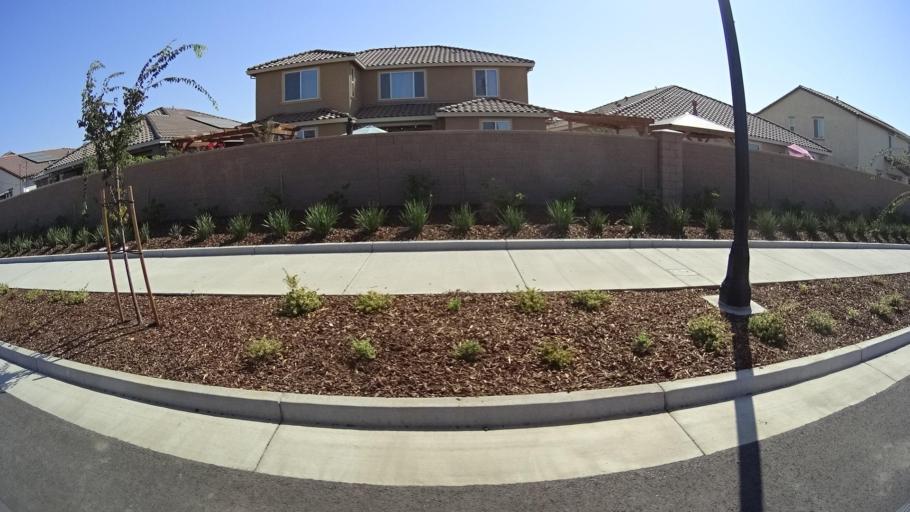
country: US
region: California
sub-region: Sacramento County
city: Elk Grove
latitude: 38.3825
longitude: -121.3806
